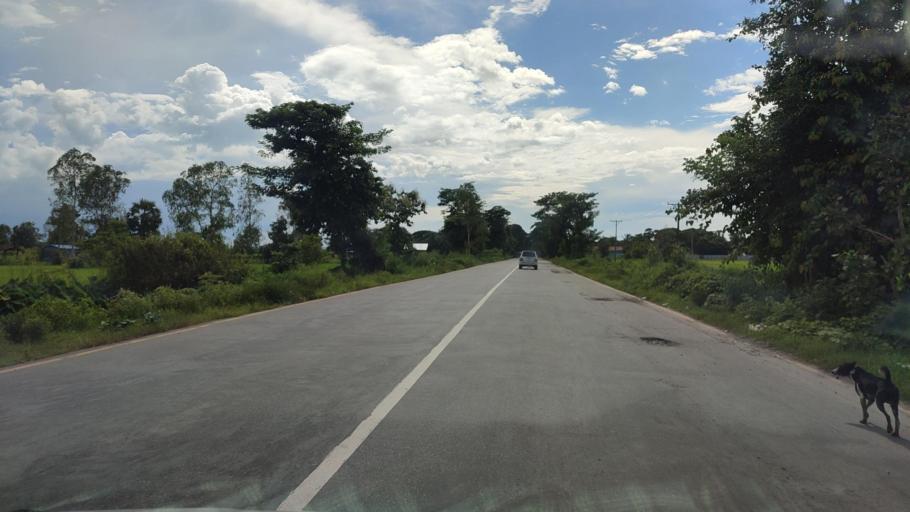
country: MM
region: Bago
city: Nyaunglebin
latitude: 18.1853
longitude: 96.5865
